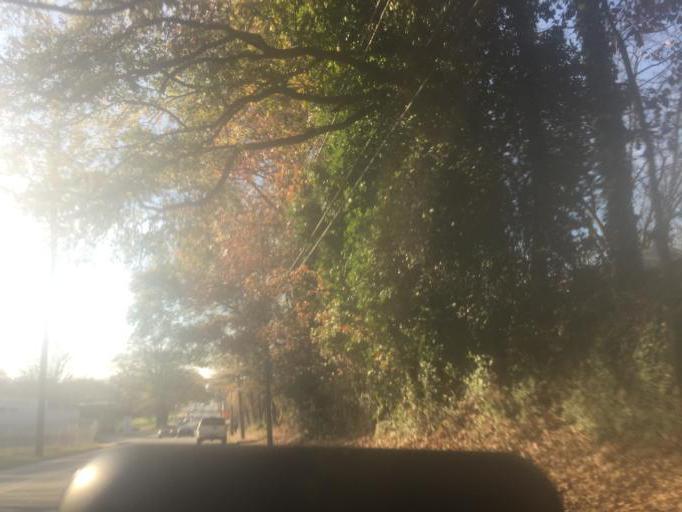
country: US
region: Georgia
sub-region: Fulton County
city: Atlanta
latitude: 33.7222
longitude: -84.4049
